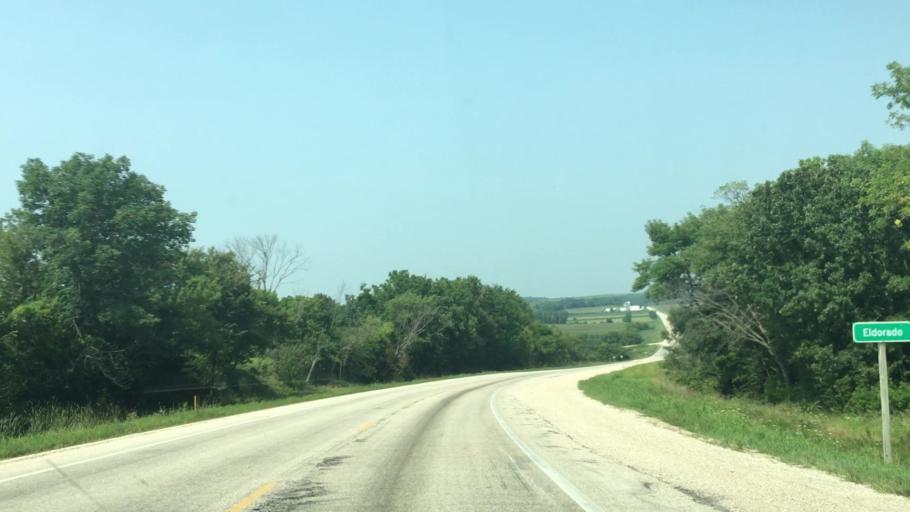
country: US
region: Iowa
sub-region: Fayette County
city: West Union
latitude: 43.0463
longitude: -91.8399
